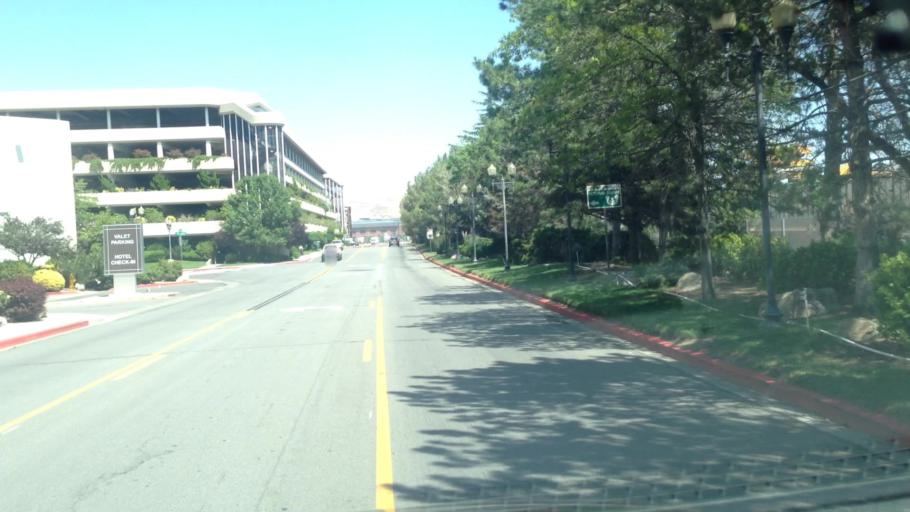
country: US
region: Nevada
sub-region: Washoe County
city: Sparks
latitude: 39.5329
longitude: -119.7581
